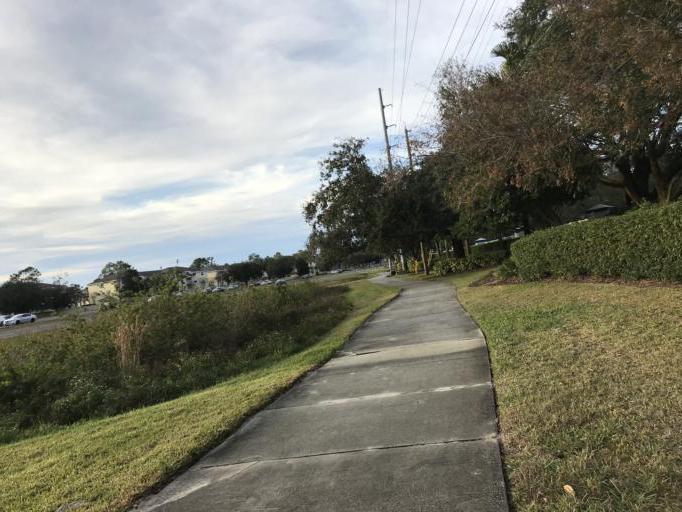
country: US
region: Florida
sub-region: Osceola County
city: Celebration
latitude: 28.3617
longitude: -81.5002
